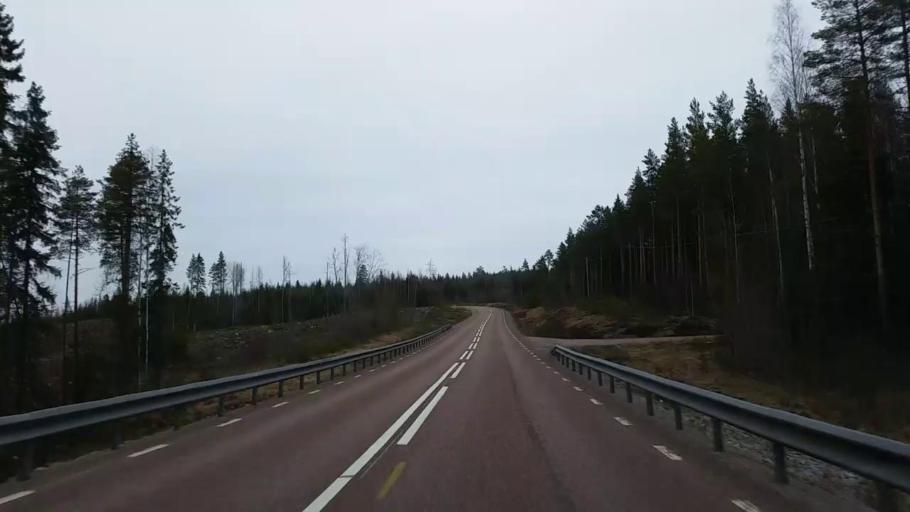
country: SE
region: Gaevleborg
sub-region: Ovanakers Kommun
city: Edsbyn
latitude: 61.2144
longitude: 15.8747
